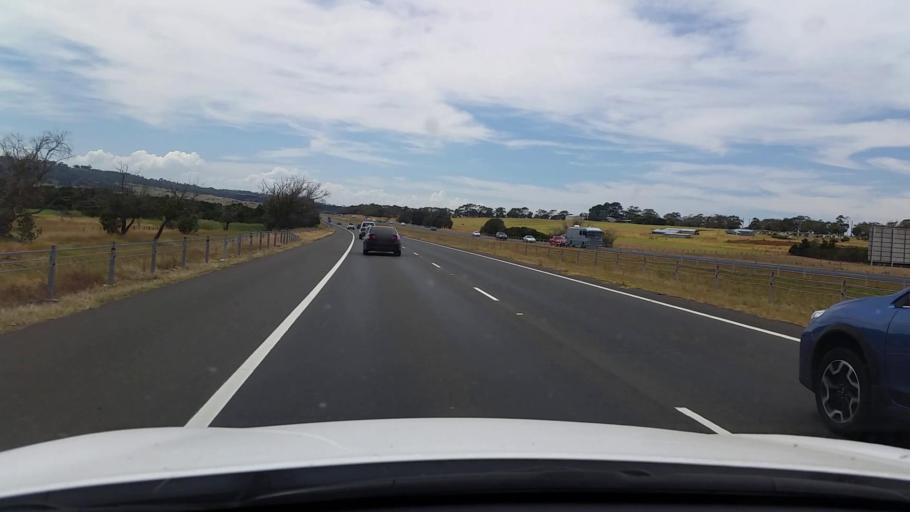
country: AU
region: Victoria
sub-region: Mornington Peninsula
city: Safety Beach
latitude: -38.3175
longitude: 145.0113
